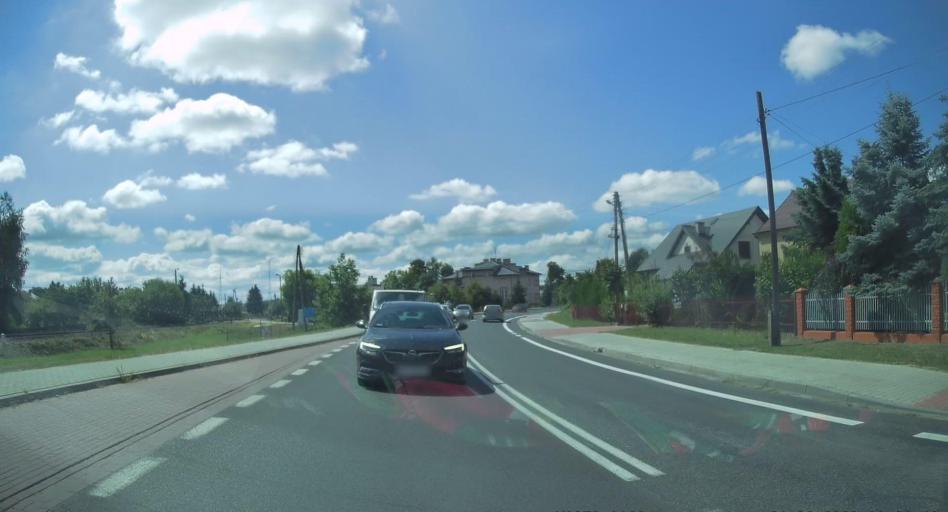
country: PL
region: Subcarpathian Voivodeship
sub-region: Powiat debicki
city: Brzeznica
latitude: 50.1030
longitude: 21.4857
